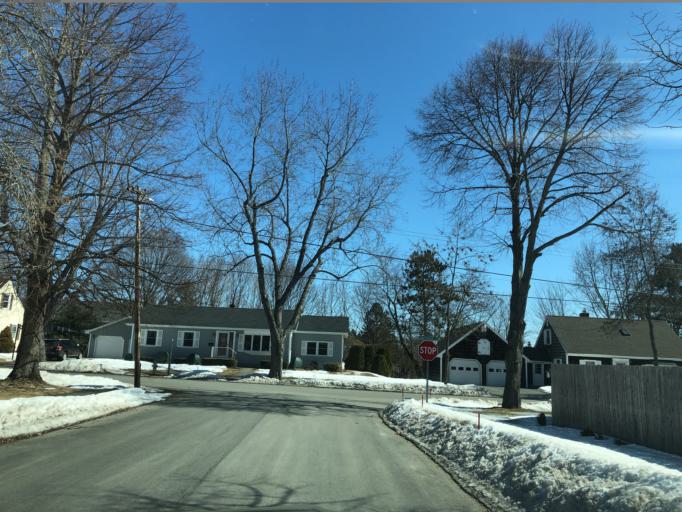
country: US
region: Maine
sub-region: Penobscot County
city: Brewer
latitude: 44.8183
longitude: -68.7539
